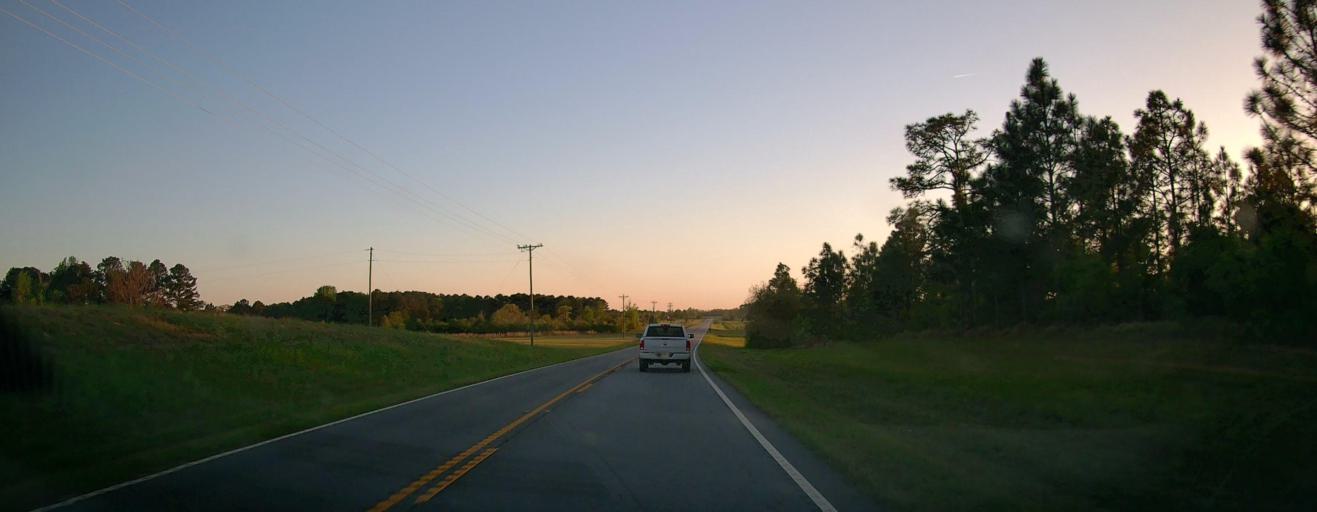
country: US
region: Georgia
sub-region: Marion County
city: Buena Vista
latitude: 32.4922
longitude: -84.6168
